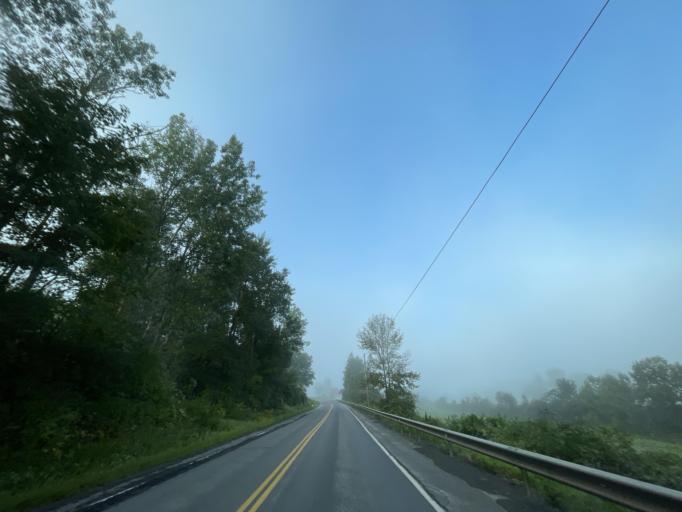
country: US
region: New York
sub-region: Chenango County
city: Oxford
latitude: 42.3668
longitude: -75.6634
